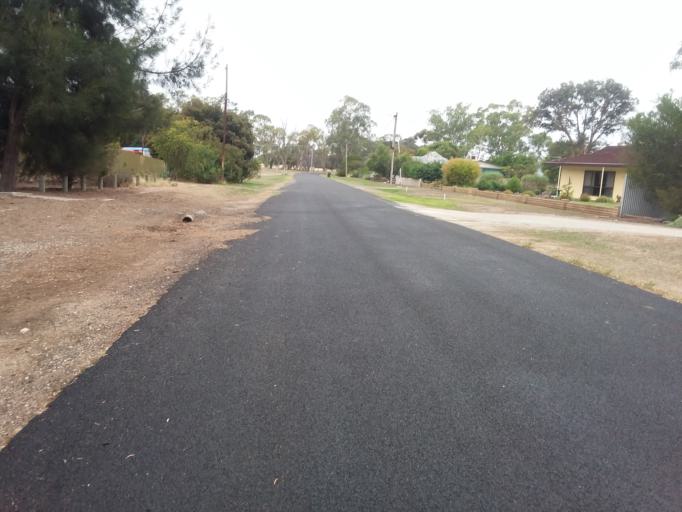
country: AU
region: Victoria
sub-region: Horsham
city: Horsham
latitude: -36.7409
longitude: 141.9378
